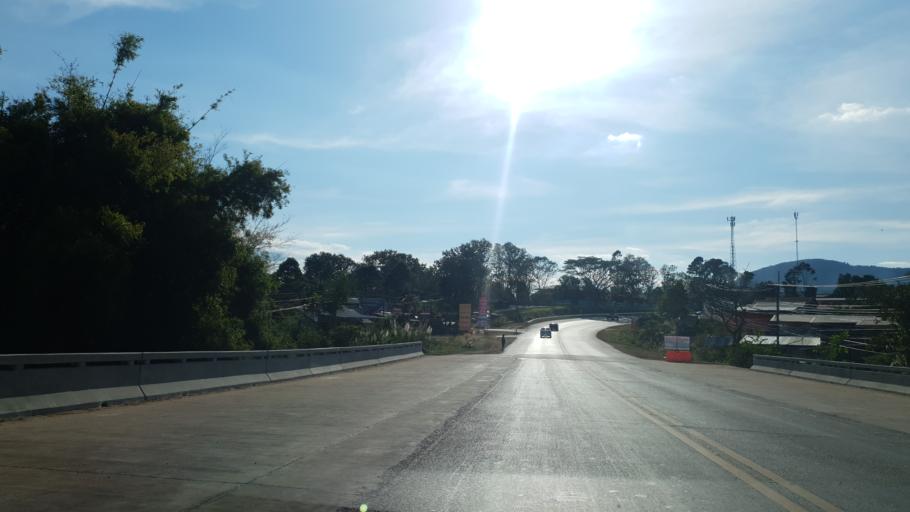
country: TH
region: Loei
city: Phu Ruea
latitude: 17.4428
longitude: 101.4735
